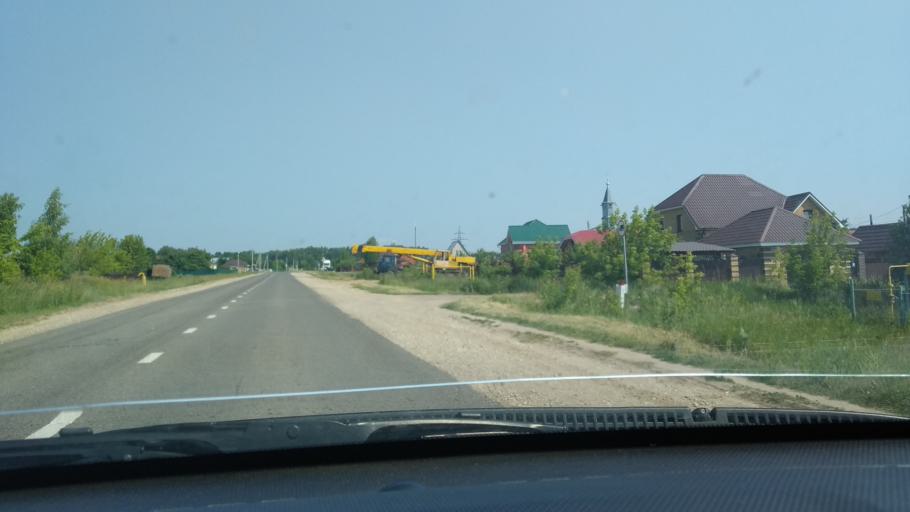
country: RU
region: Tatarstan
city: Osinovo
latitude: 55.9824
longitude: 48.8126
